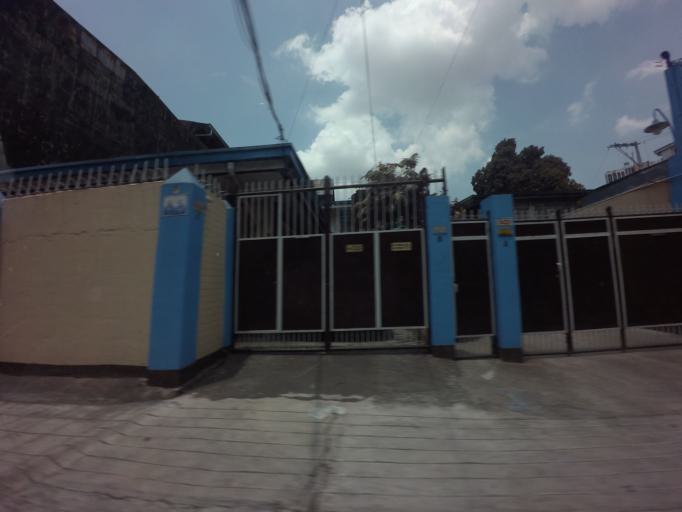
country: PH
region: Metro Manila
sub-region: Makati City
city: Makati City
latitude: 14.5631
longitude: 121.0335
